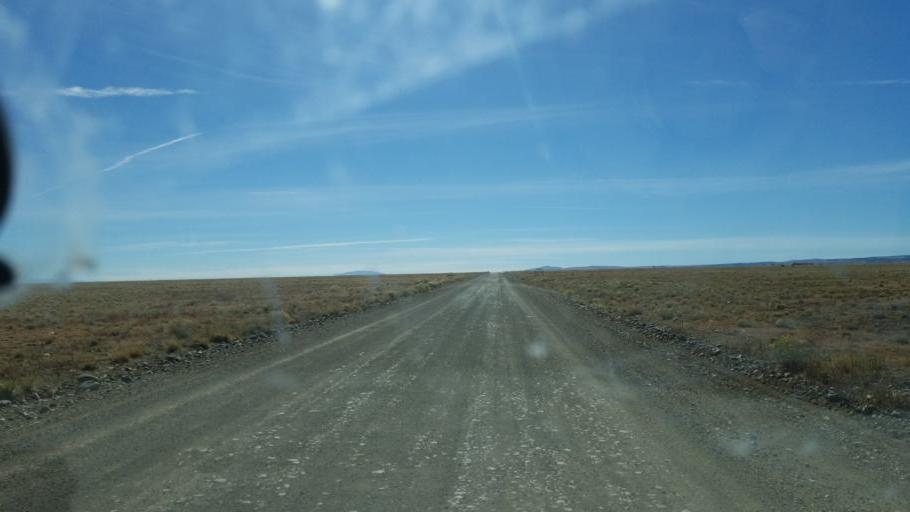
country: US
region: Colorado
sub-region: Rio Grande County
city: Monte Vista
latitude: 37.3670
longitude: -106.1493
